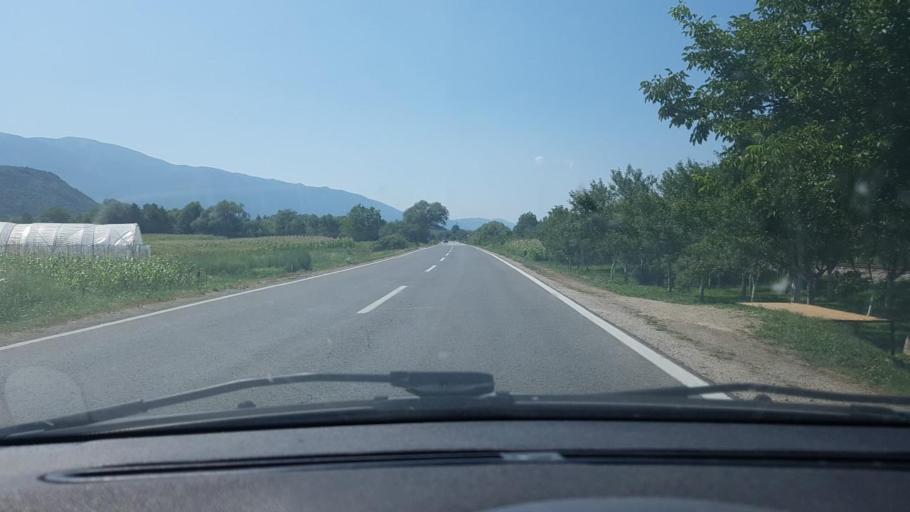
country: BA
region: Federation of Bosnia and Herzegovina
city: Bihac
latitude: 44.8048
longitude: 15.8995
